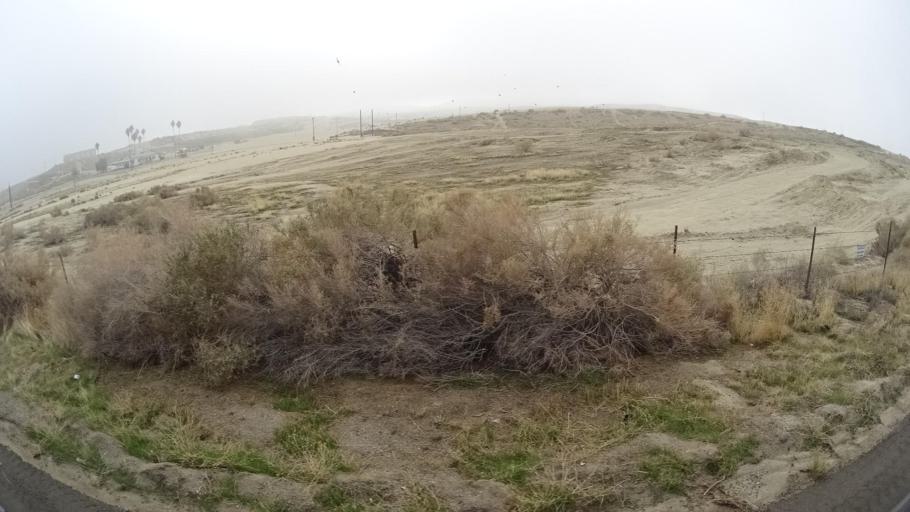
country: US
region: California
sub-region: Kern County
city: Ford City
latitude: 35.1651
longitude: -119.3831
